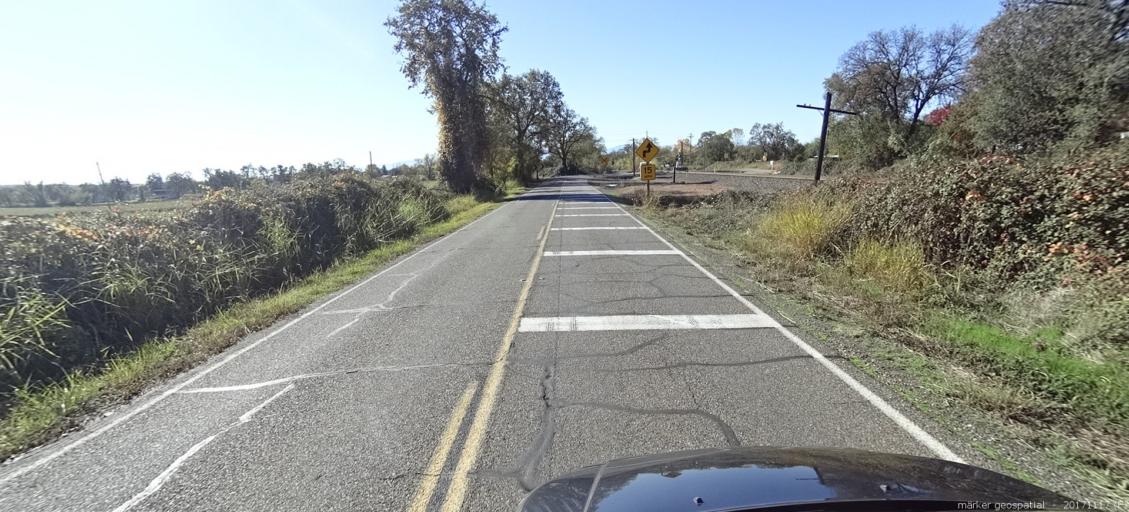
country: US
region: California
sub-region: Shasta County
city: Cottonwood
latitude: 40.3977
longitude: -122.2520
